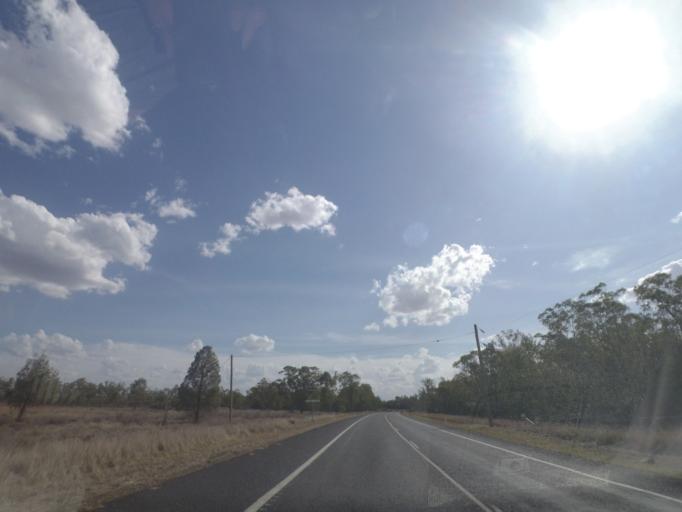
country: AU
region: New South Wales
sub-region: Moree Plains
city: Boggabilla
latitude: -28.5360
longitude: 150.8917
